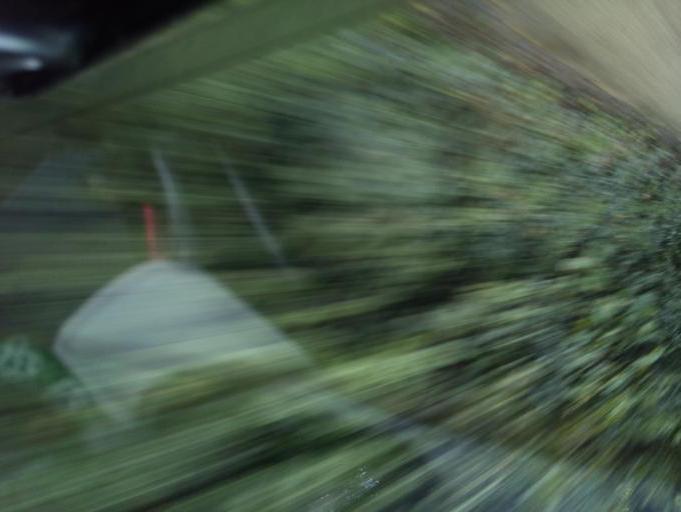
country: GB
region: England
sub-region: Devon
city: Modbury
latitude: 50.3394
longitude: -3.8591
